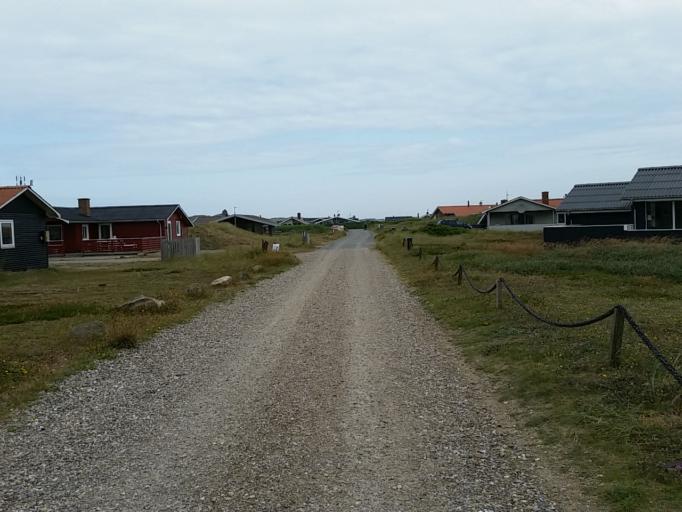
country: DK
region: Central Jutland
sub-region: Ringkobing-Skjern Kommune
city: Hvide Sande
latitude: 55.8659
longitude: 8.1646
